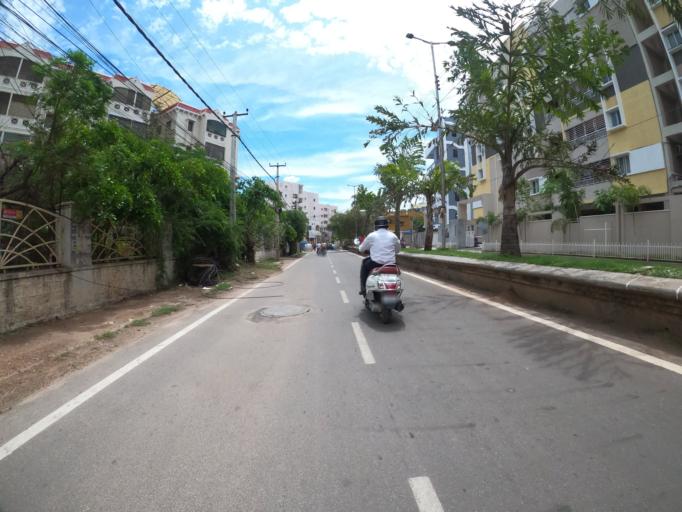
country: IN
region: Telangana
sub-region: Hyderabad
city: Hyderabad
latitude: 17.3662
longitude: 78.4220
